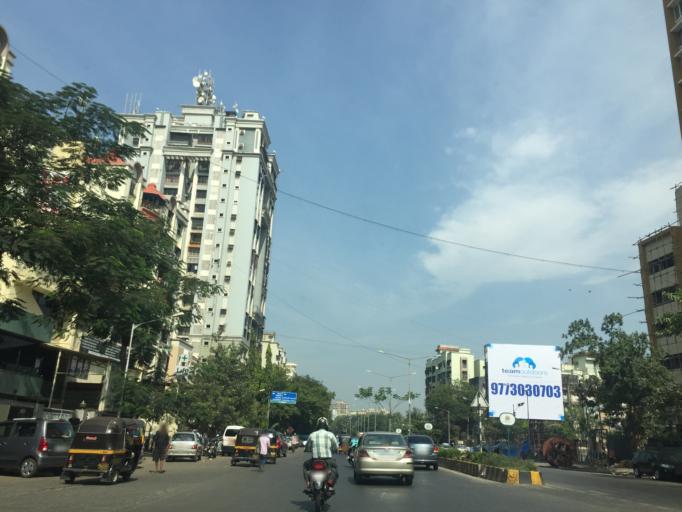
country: IN
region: Maharashtra
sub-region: Mumbai Suburban
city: Borivli
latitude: 19.2273
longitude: 72.8408
